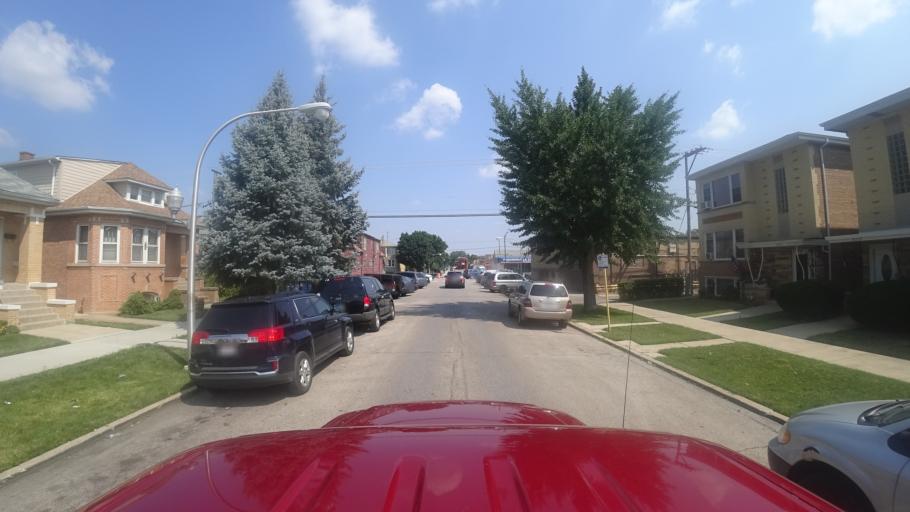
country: US
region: Illinois
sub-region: Cook County
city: Cicero
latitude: 41.8073
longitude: -87.7274
